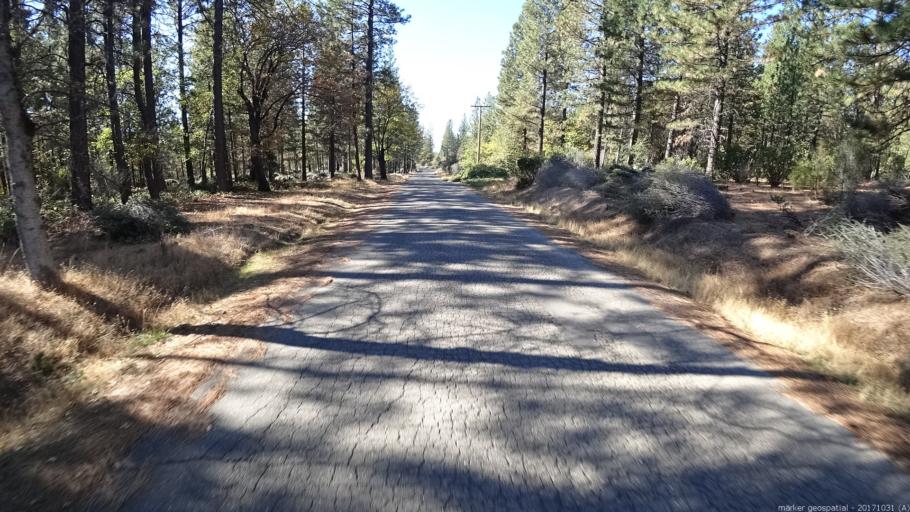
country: US
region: California
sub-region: Shasta County
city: Shingletown
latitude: 40.4469
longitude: -121.8136
